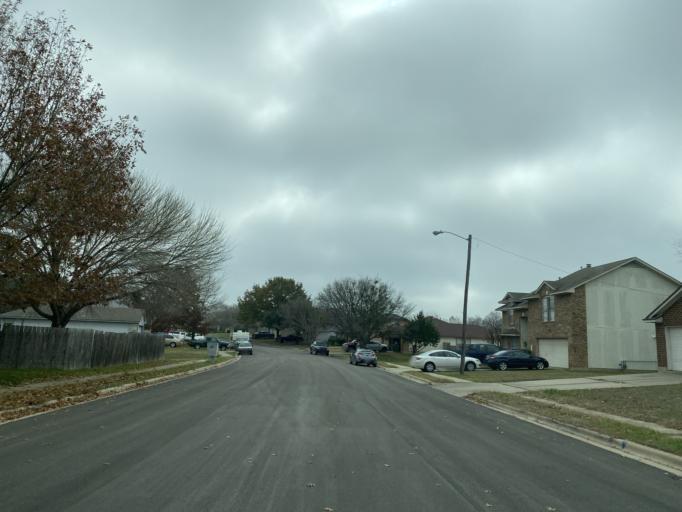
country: US
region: Texas
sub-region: Williamson County
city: Round Rock
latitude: 30.5346
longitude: -97.6789
